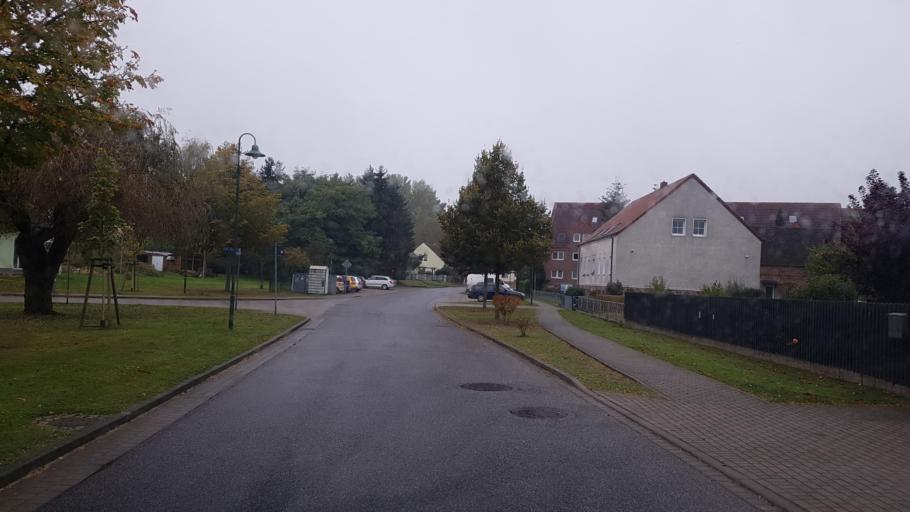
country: DE
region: Brandenburg
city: Furstenwalde
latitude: 52.4295
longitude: 14.0378
